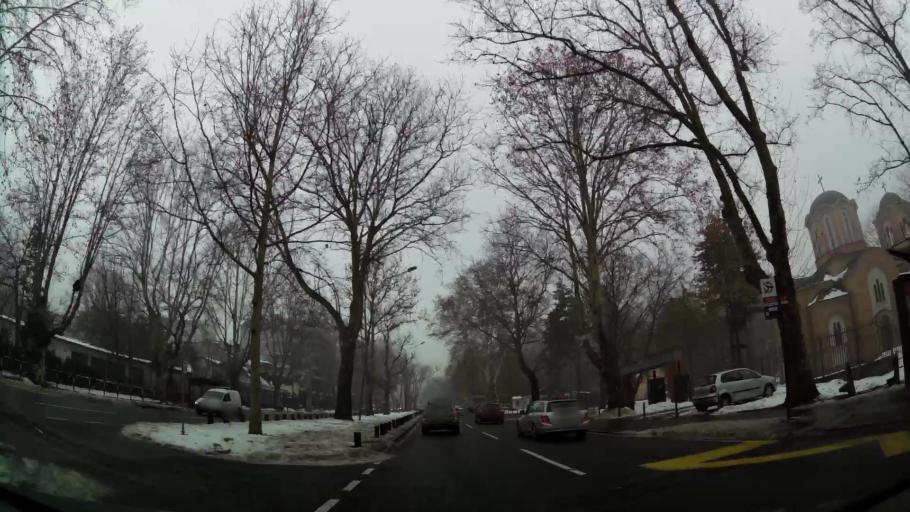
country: RS
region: Central Serbia
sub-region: Belgrade
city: Vozdovac
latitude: 44.7624
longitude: 20.4793
